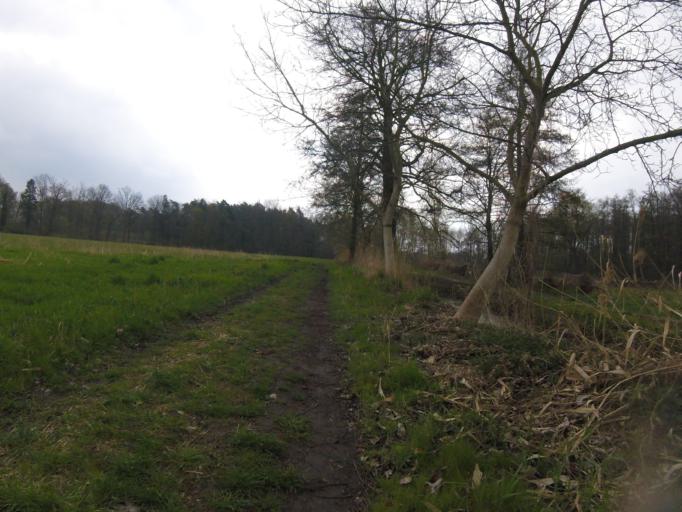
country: DE
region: Brandenburg
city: Konigs Wusterhausen
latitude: 52.2836
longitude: 13.6002
